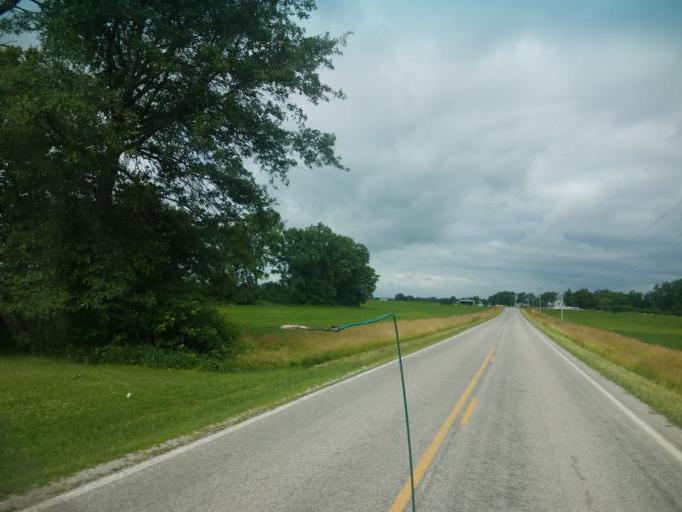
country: US
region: Ohio
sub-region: Union County
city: Richwood
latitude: 40.4050
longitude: -83.4413
